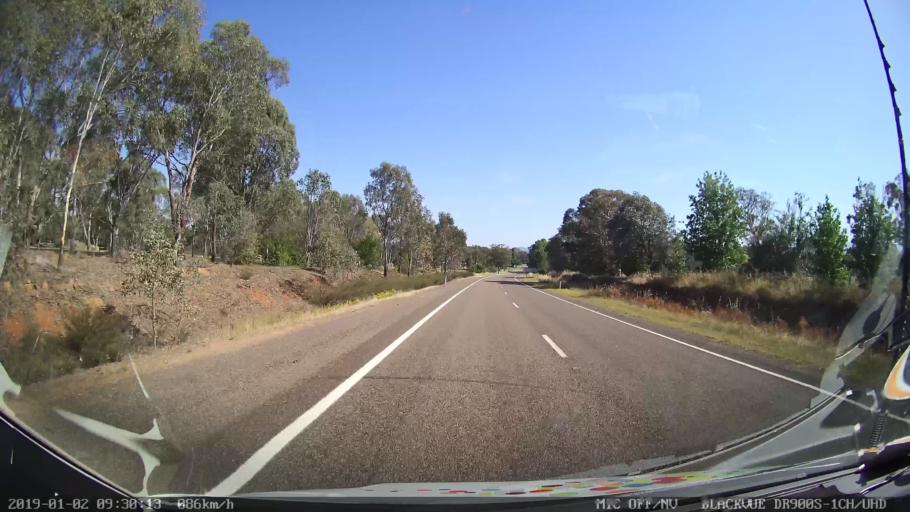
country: AU
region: New South Wales
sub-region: Tumut Shire
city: Tumut
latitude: -35.3291
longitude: 148.2376
